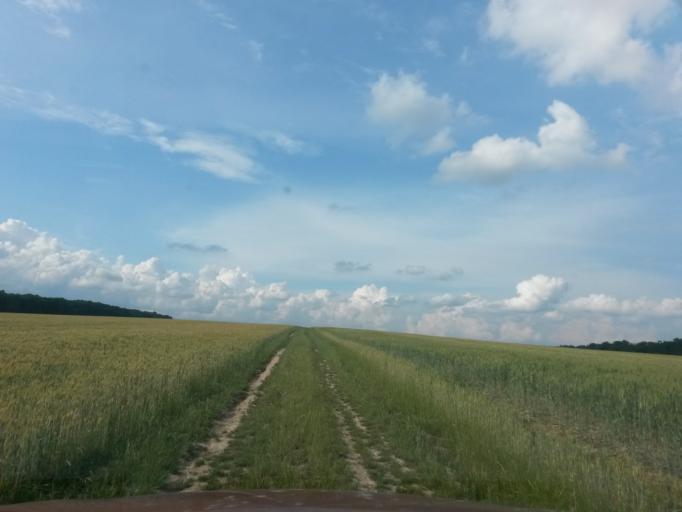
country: SK
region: Kosicky
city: Moldava nad Bodvou
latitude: 48.6260
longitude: 21.1036
